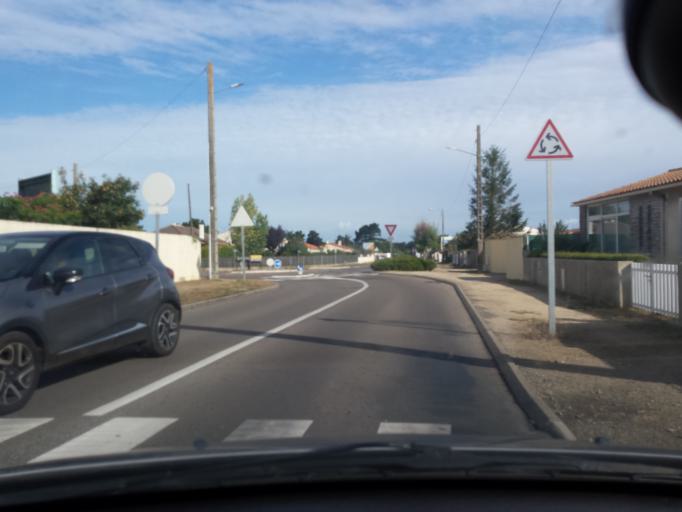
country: FR
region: Pays de la Loire
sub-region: Departement de la Vendee
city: Olonne-sur-Mer
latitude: 46.5464
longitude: -1.8040
